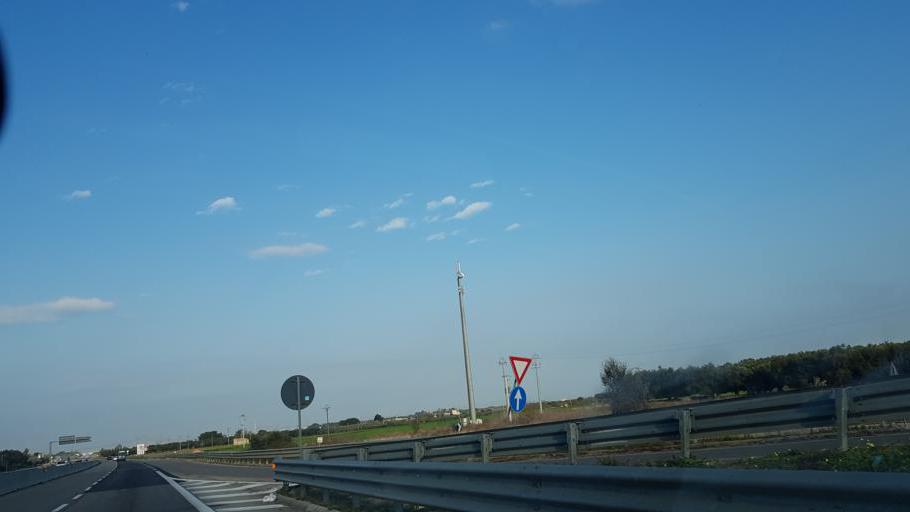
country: IT
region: Apulia
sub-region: Provincia di Brindisi
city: Mesagne
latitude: 40.5918
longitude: 17.8615
